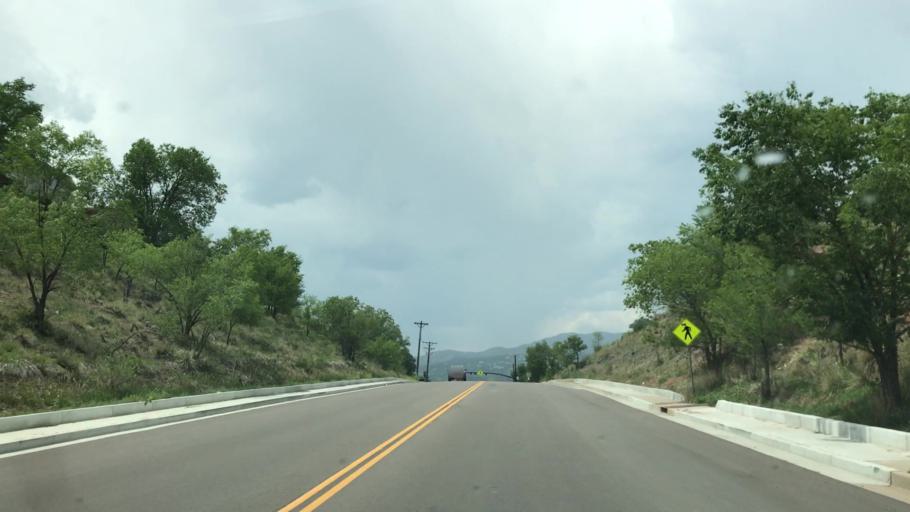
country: US
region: Colorado
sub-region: El Paso County
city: Colorado Springs
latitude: 38.8513
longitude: -104.8602
